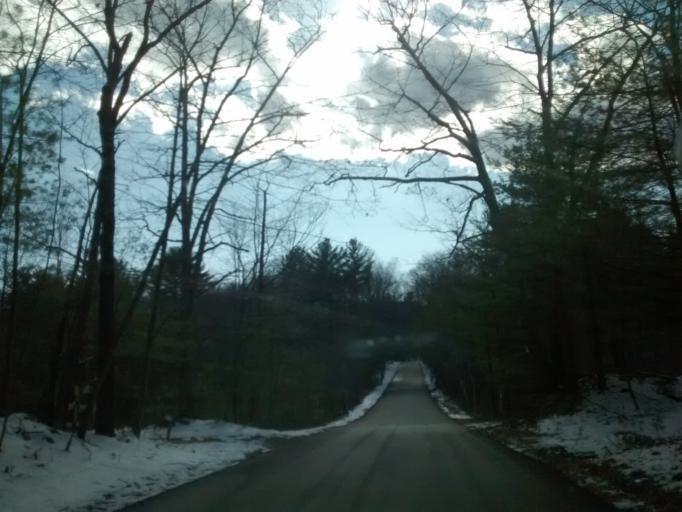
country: US
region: Massachusetts
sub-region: Worcester County
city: East Douglas
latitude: 42.0445
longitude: -71.6799
